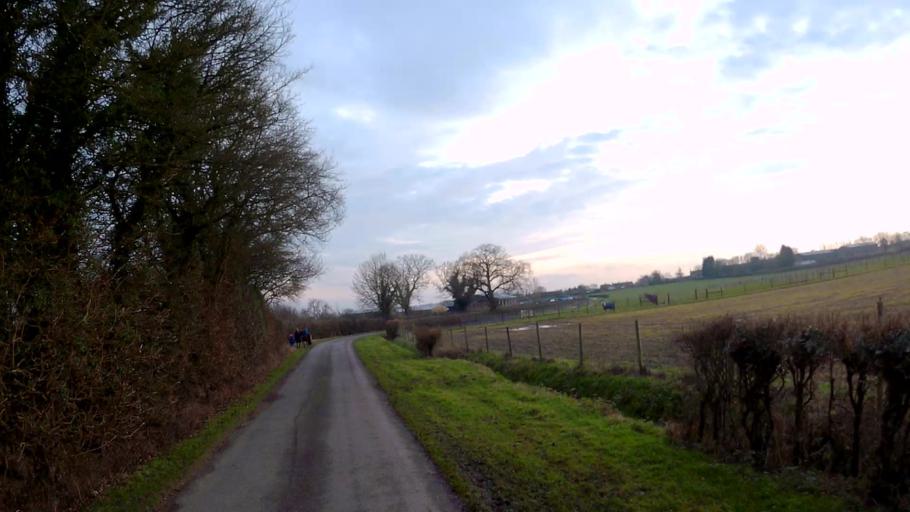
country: GB
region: England
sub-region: Lincolnshire
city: Bourne
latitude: 52.8171
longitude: -0.3991
